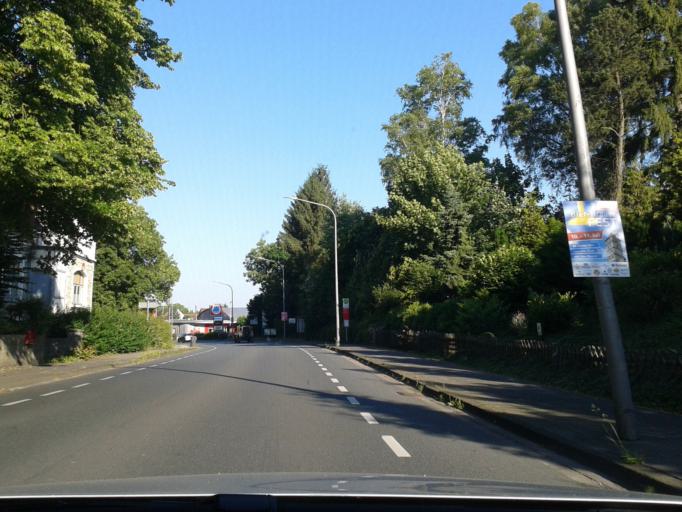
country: DE
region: North Rhine-Westphalia
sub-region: Regierungsbezirk Detmold
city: Lemgo
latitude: 52.0265
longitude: 8.9213
